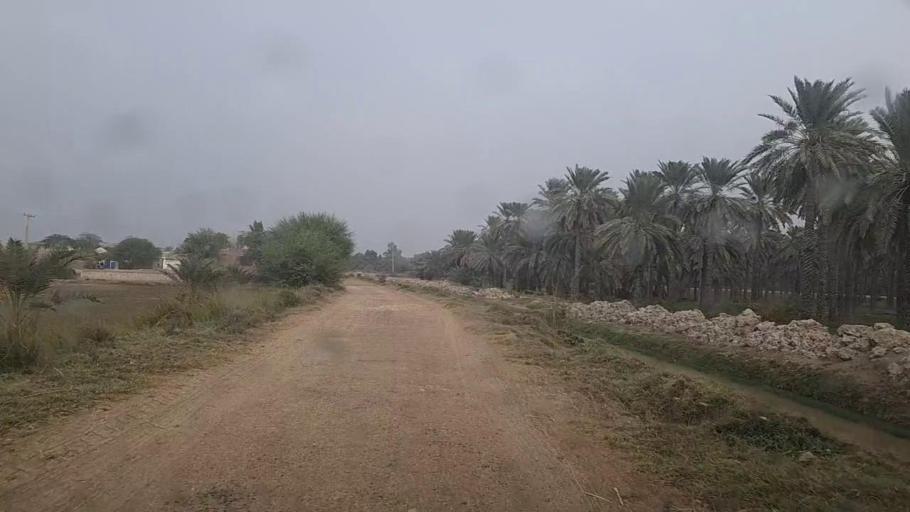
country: PK
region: Sindh
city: Gambat
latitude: 27.3906
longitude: 68.5954
